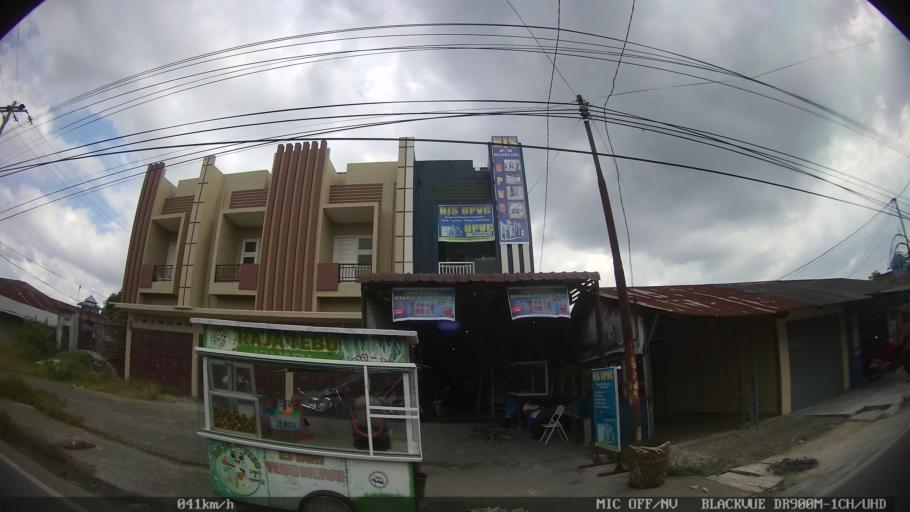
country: ID
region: North Sumatra
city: Sunggal
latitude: 3.6187
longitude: 98.6060
